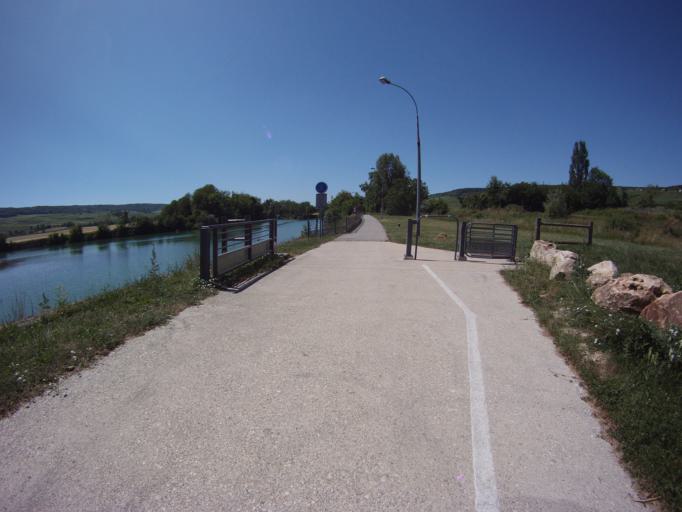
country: FR
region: Champagne-Ardenne
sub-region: Departement de la Marne
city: Damery
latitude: 49.0757
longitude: 3.8403
